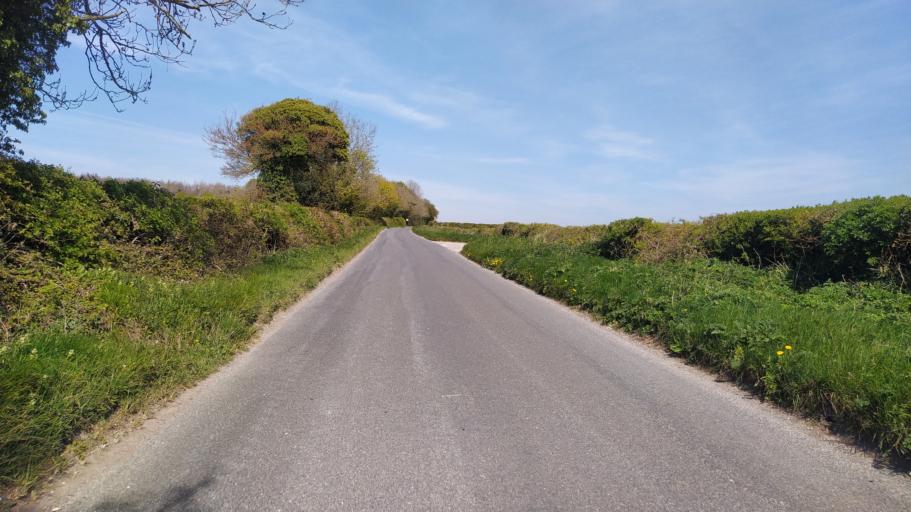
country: GB
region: England
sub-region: Dorset
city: Blandford Forum
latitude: 50.8822
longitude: -2.1835
